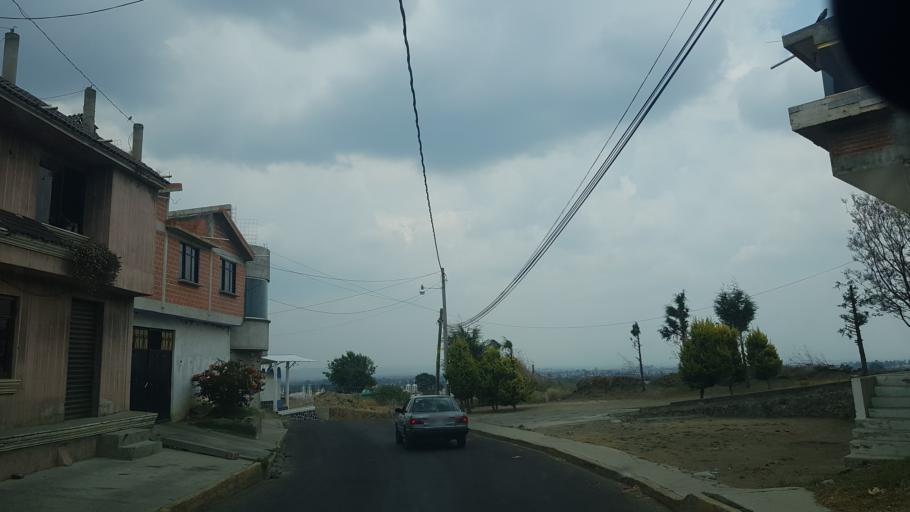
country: MX
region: Puebla
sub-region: Huejotzingo
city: San Miguel Tianguizolco
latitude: 19.1592
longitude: -98.4382
